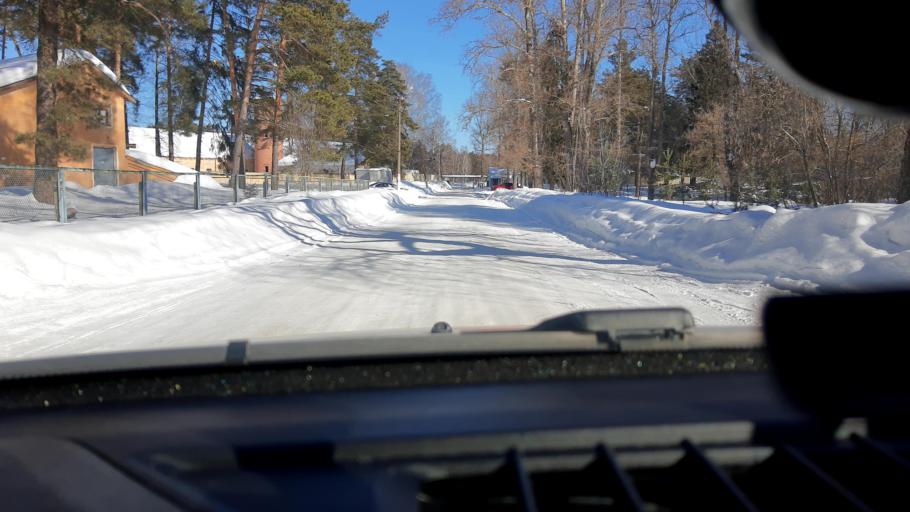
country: RU
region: Nizjnij Novgorod
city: Yuganets
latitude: 56.2482
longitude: 43.2332
